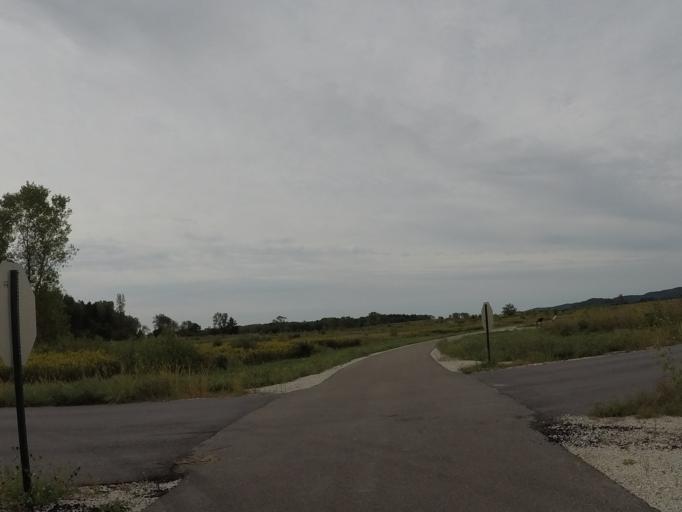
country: US
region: Wisconsin
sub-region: Sauk County
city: Prairie du Sac
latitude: 43.3693
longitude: -89.7360
